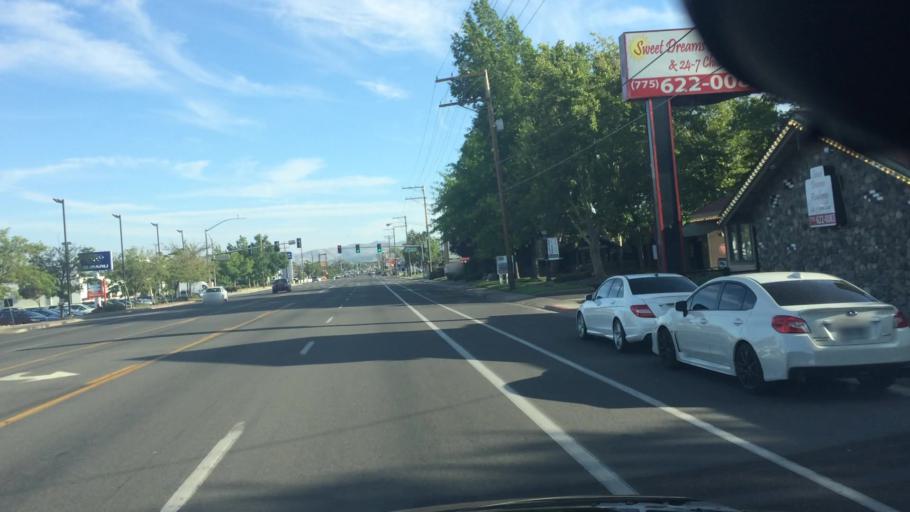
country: US
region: Nevada
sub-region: Washoe County
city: Reno
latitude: 39.5021
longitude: -119.7892
